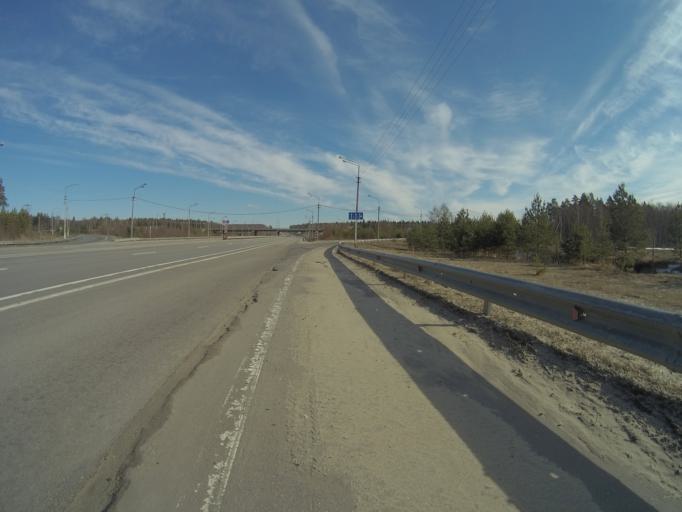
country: RU
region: Vladimir
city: Kommunar
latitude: 56.0816
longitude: 40.4689
